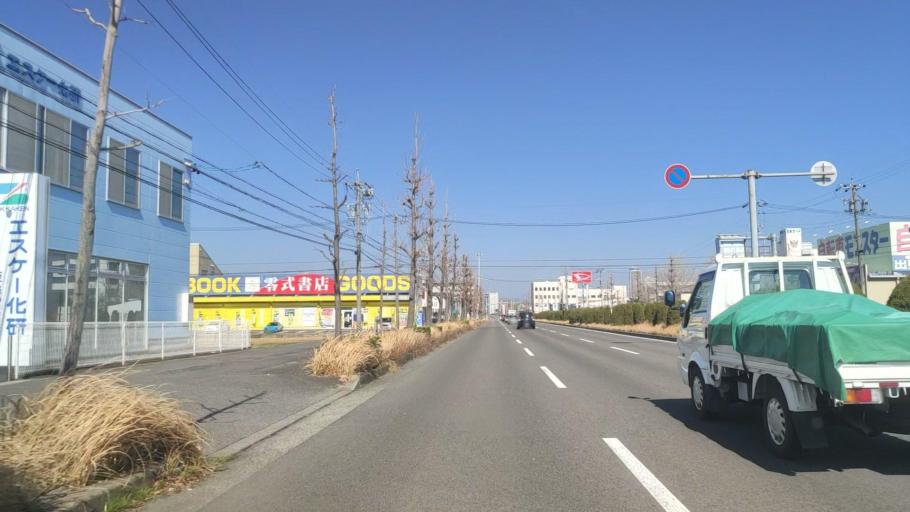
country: JP
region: Gifu
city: Kasamatsucho
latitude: 35.3899
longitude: 136.7474
